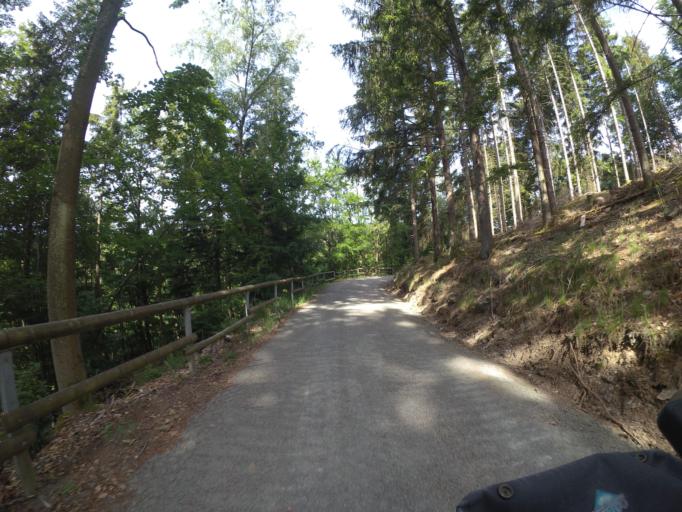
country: DE
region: Saarland
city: Nonnweiler
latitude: 49.6266
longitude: 6.9388
